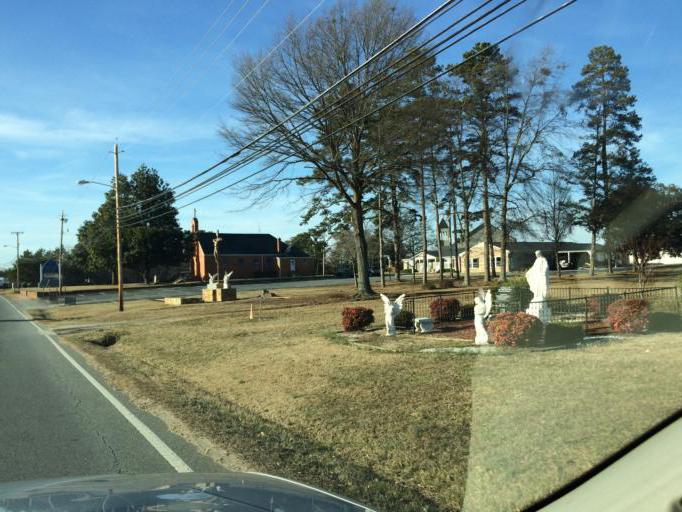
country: US
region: North Carolina
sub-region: Rutherford County
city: Forest City
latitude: 35.3486
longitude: -81.8878
